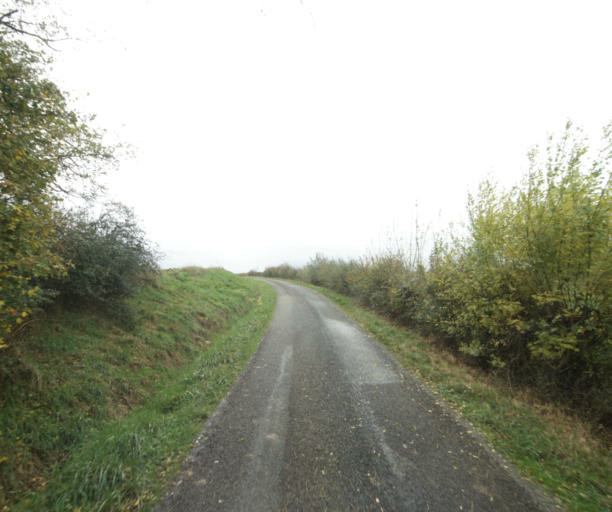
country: FR
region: Rhone-Alpes
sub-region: Departement de l'Ain
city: Pont-de-Vaux
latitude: 46.4710
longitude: 4.8784
